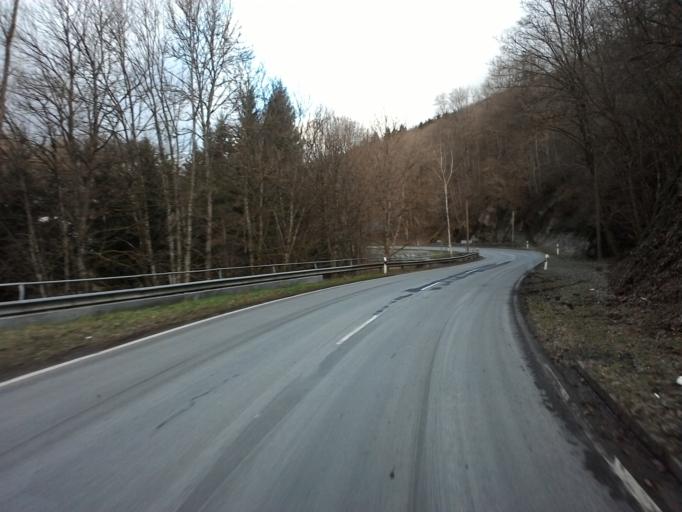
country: DE
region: Rheinland-Pfalz
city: Niederraden
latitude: 49.9964
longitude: 6.3057
